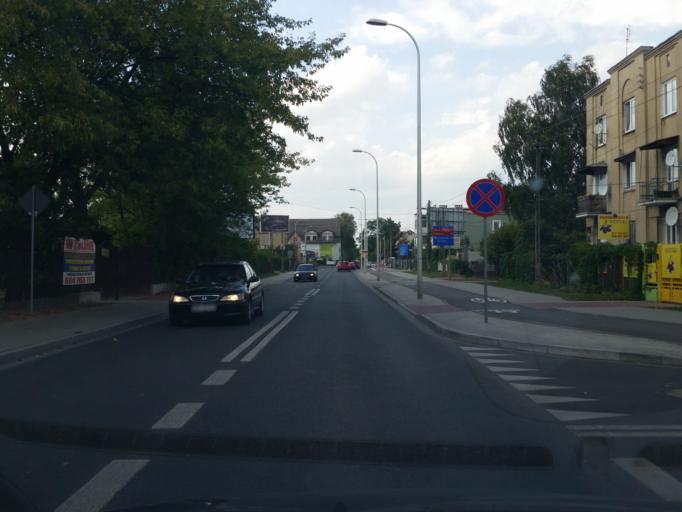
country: PL
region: Masovian Voivodeship
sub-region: Warszawa
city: Ursus
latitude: 52.1990
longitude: 20.9169
